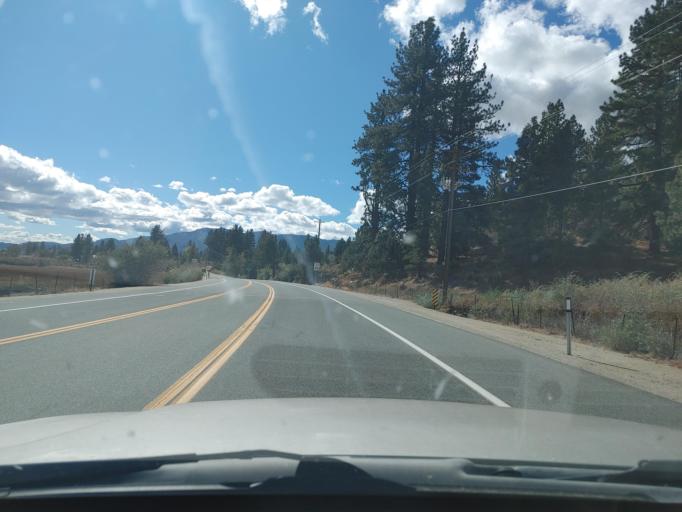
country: US
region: Nevada
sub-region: Carson City
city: Carson City
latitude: 39.3030
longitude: -119.8287
